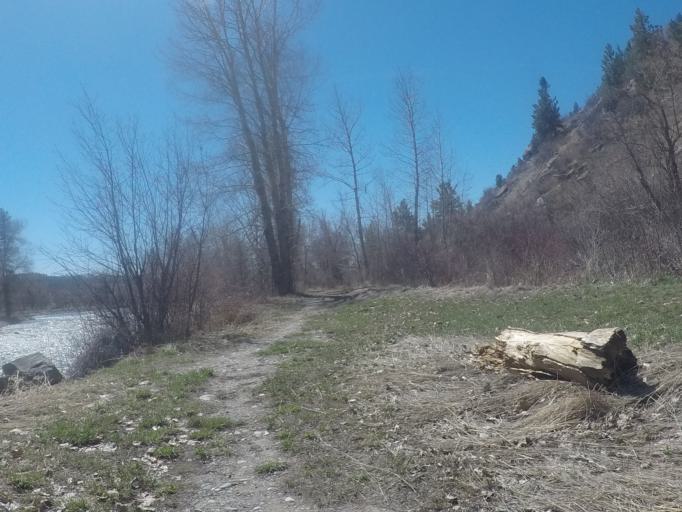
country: US
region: Montana
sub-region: Stillwater County
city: Columbus
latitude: 45.6222
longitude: -109.2902
